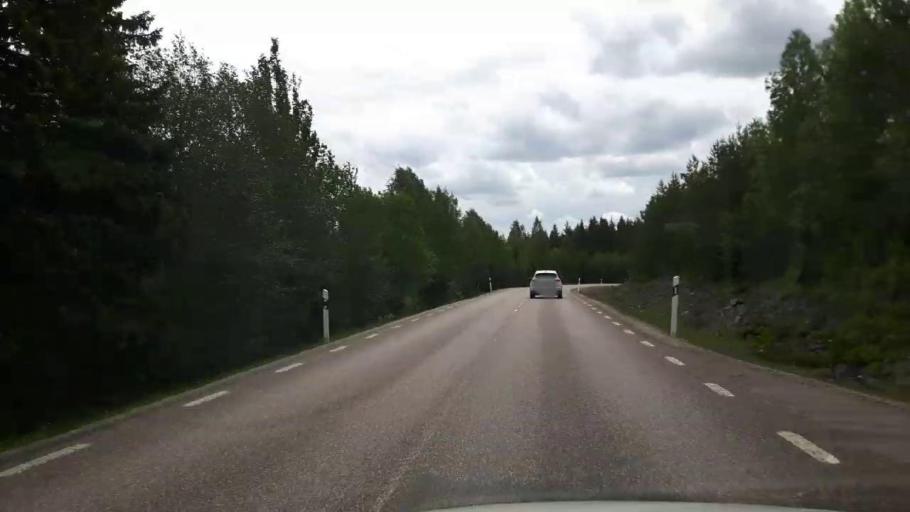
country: SE
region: Vaestmanland
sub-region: Norbergs Kommun
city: Norberg
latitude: 60.1350
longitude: 15.9430
